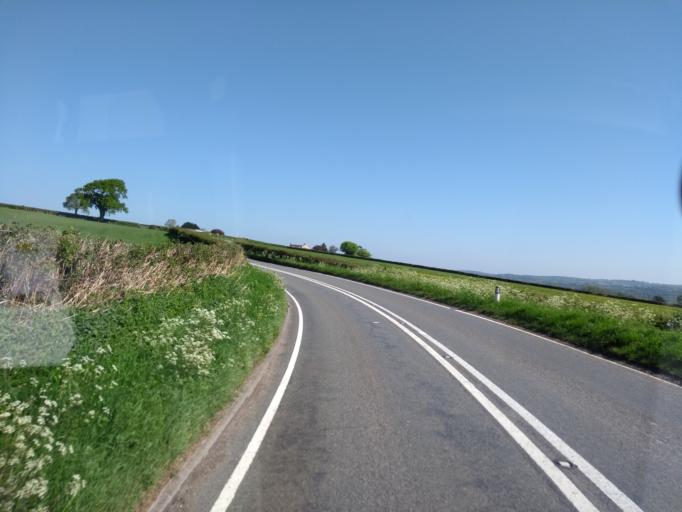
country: GB
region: England
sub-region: Somerset
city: Chard
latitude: 50.8319
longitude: -2.9626
